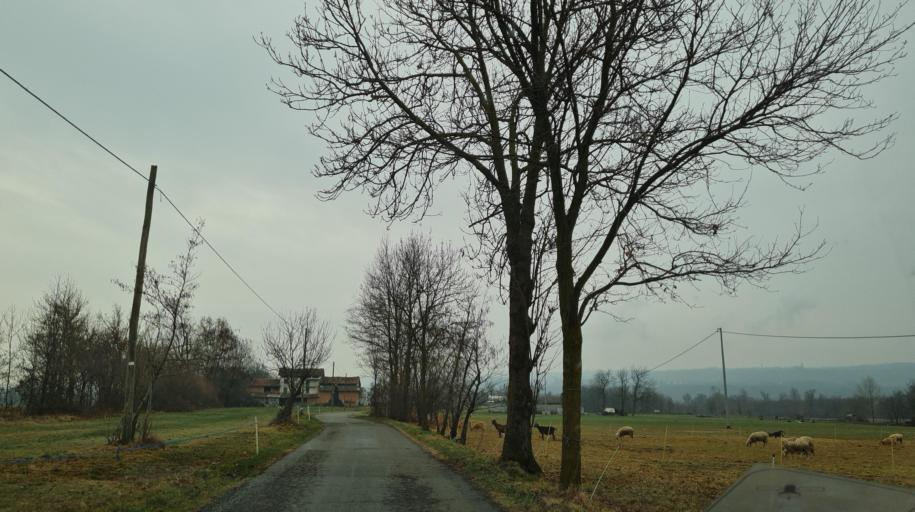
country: IT
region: Piedmont
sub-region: Provincia di Biella
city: Ceresane-Curanuova
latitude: 45.5250
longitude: 8.0269
